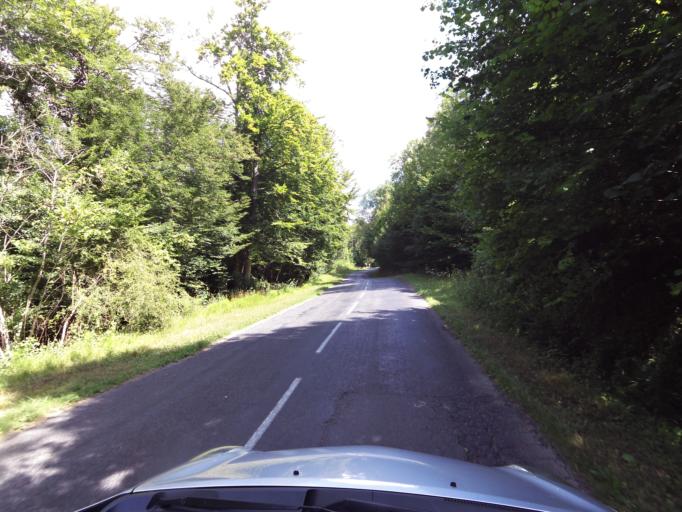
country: FR
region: Picardie
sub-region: Departement de l'Aisne
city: Villers-Cotterets
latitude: 49.2532
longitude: 3.1760
